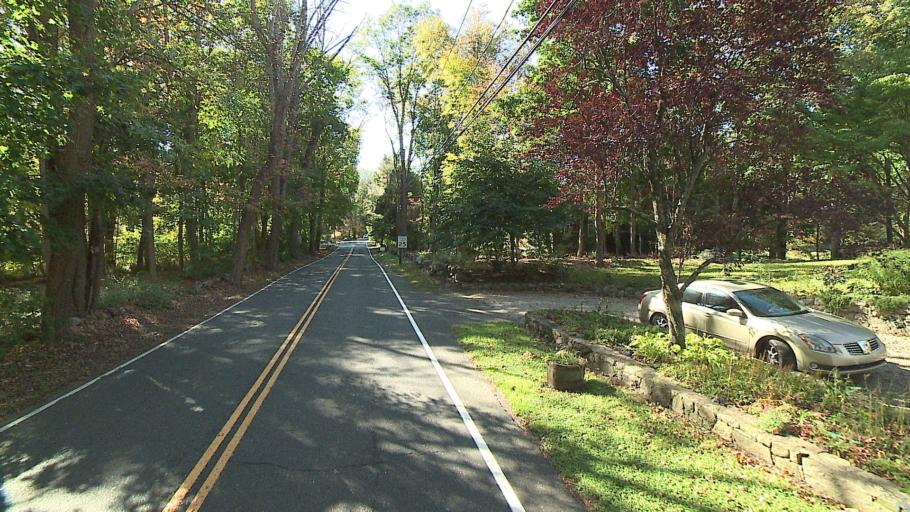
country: US
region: Connecticut
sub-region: Fairfield County
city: Westport
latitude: 41.1893
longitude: -73.3397
